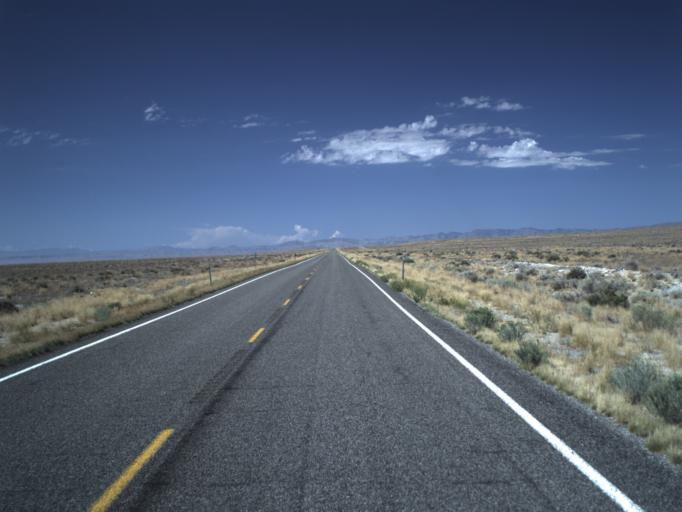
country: US
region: Utah
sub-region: Millard County
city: Delta
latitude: 39.1630
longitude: -113.0474
